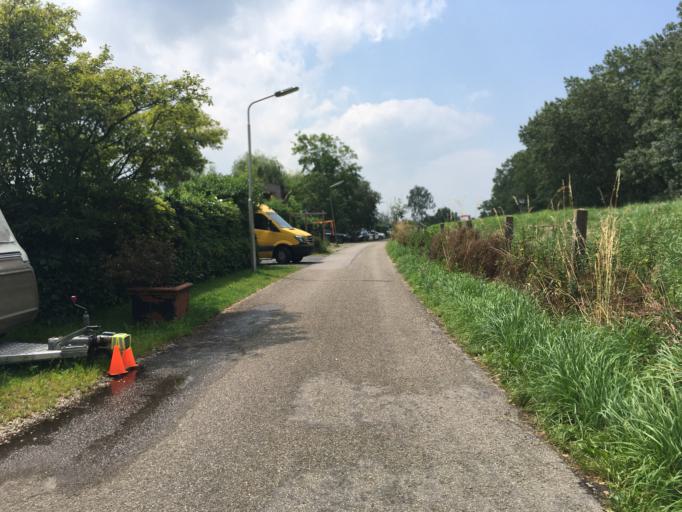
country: NL
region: North Holland
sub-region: Gemeente Zaanstad
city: Zaanstad
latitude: 52.3889
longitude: 4.7523
